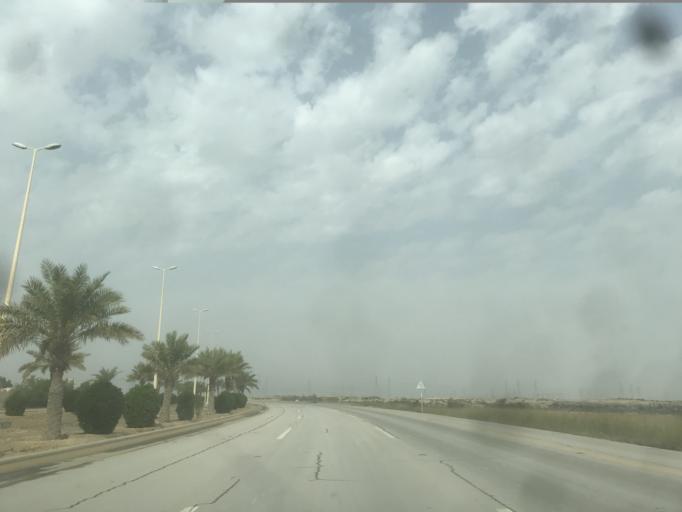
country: SA
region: Eastern Province
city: Dhahran
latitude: 26.2002
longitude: 50.0420
